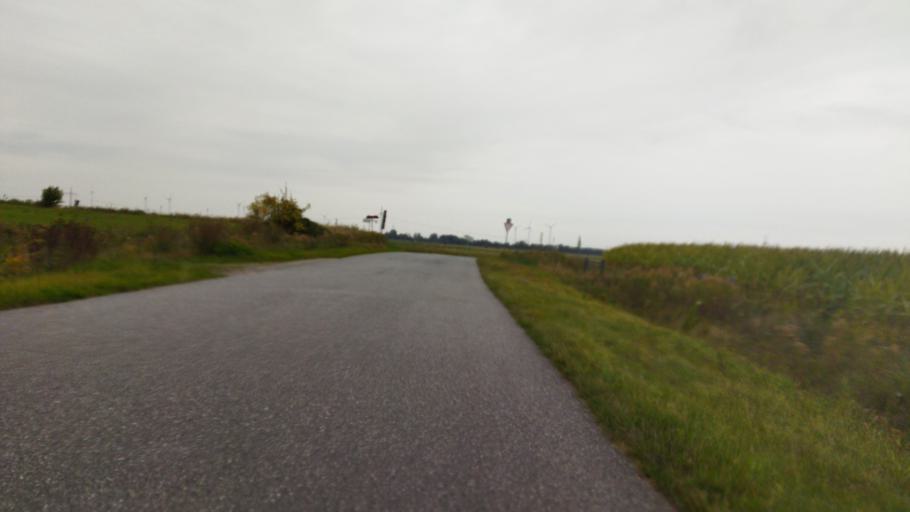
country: DE
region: Lower Saxony
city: Jemgum
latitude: 53.3258
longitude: 7.3027
